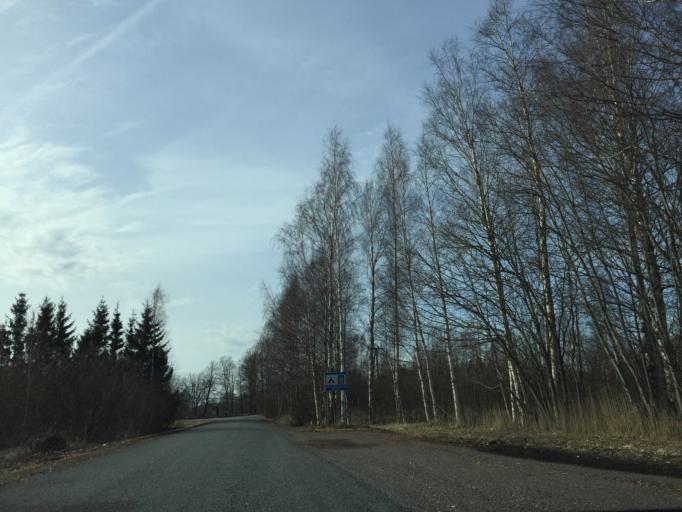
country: EE
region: Paernumaa
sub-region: Paernu linn
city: Parnu
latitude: 58.2463
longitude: 24.5057
